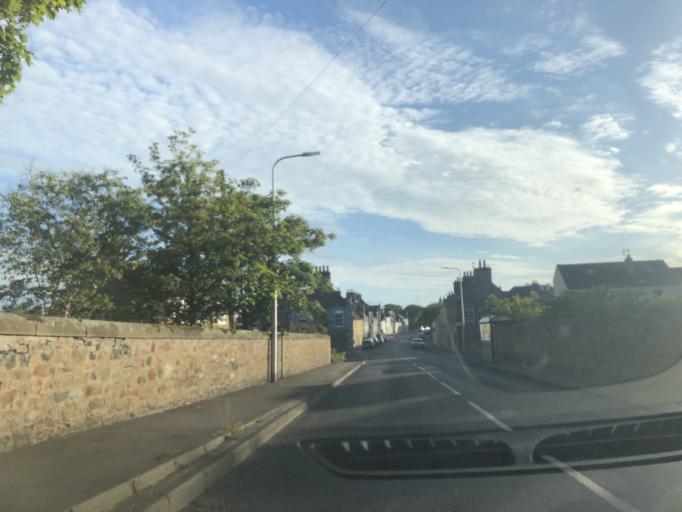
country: GB
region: Scotland
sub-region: Fife
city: Saint Monance
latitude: 56.1916
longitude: -2.8150
